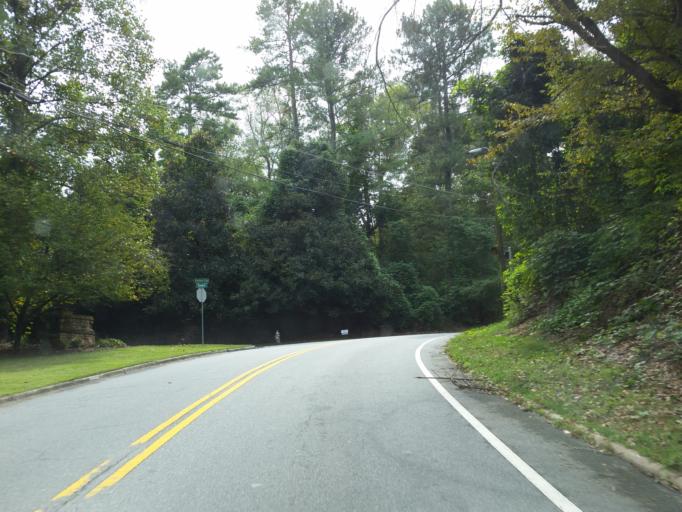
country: US
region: Georgia
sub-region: Fulton County
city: Sandy Springs
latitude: 33.9451
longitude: -84.3993
